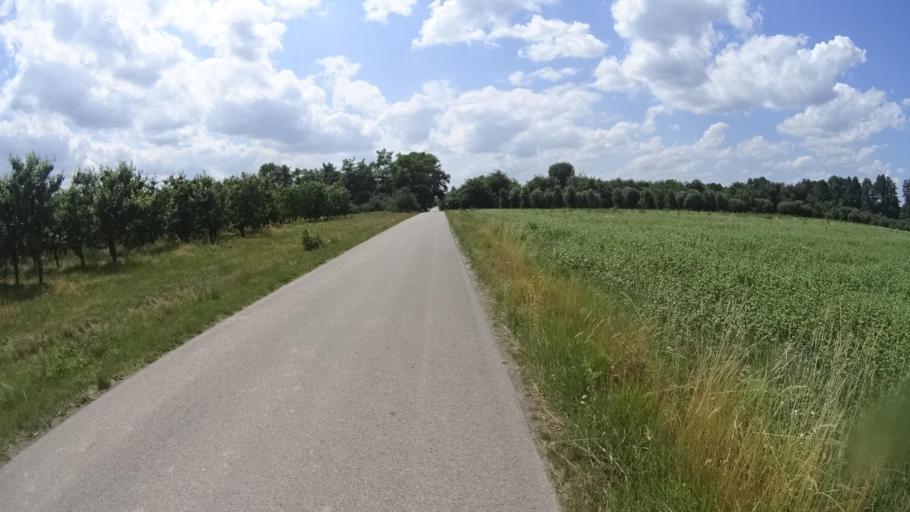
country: PL
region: Masovian Voivodeship
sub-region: Powiat grojecki
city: Goszczyn
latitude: 51.7148
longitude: 20.8949
